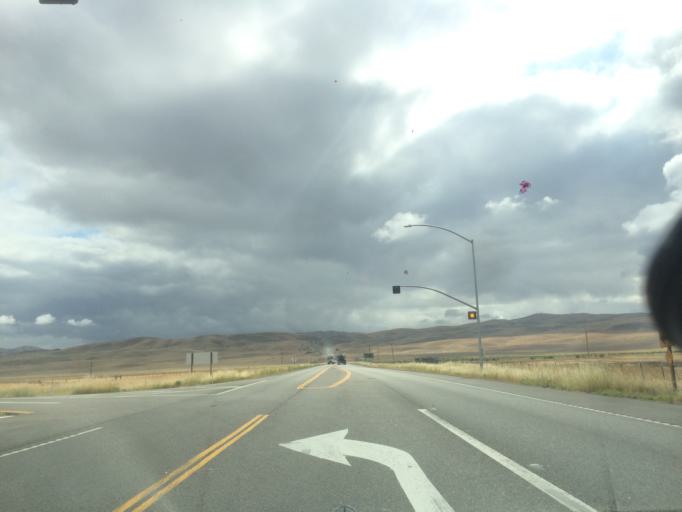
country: US
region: California
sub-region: San Luis Obispo County
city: Shandon
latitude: 35.7344
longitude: -120.2847
